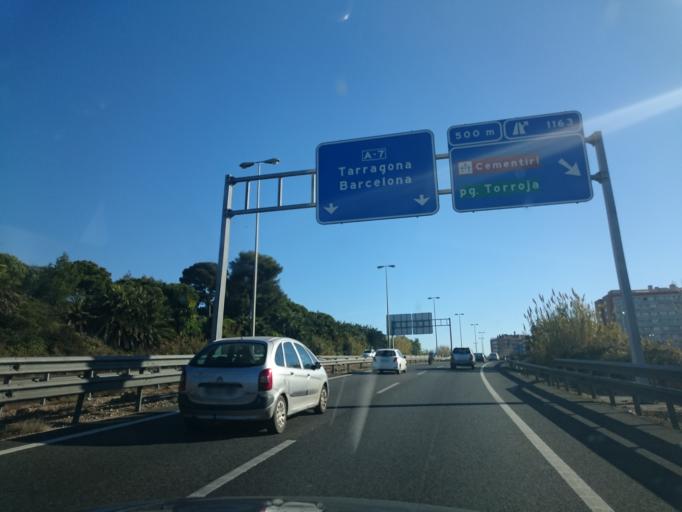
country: ES
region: Catalonia
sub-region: Provincia de Tarragona
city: Tarragona
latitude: 41.1242
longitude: 1.2494
